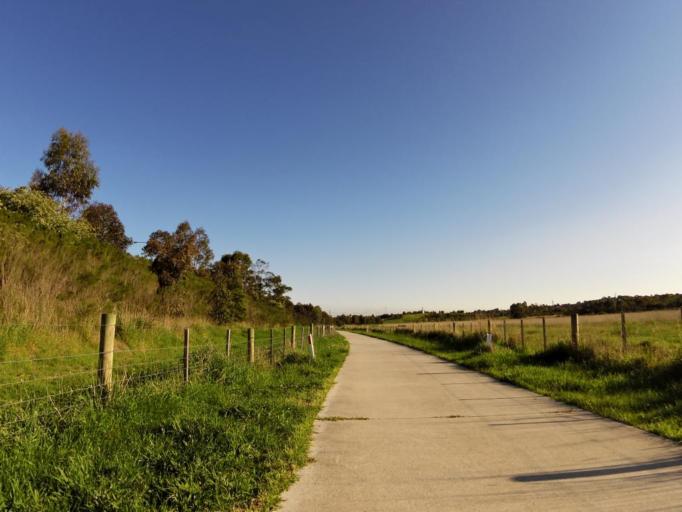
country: AU
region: Victoria
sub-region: Monash
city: Mulgrave
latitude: -37.9188
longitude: 145.2146
